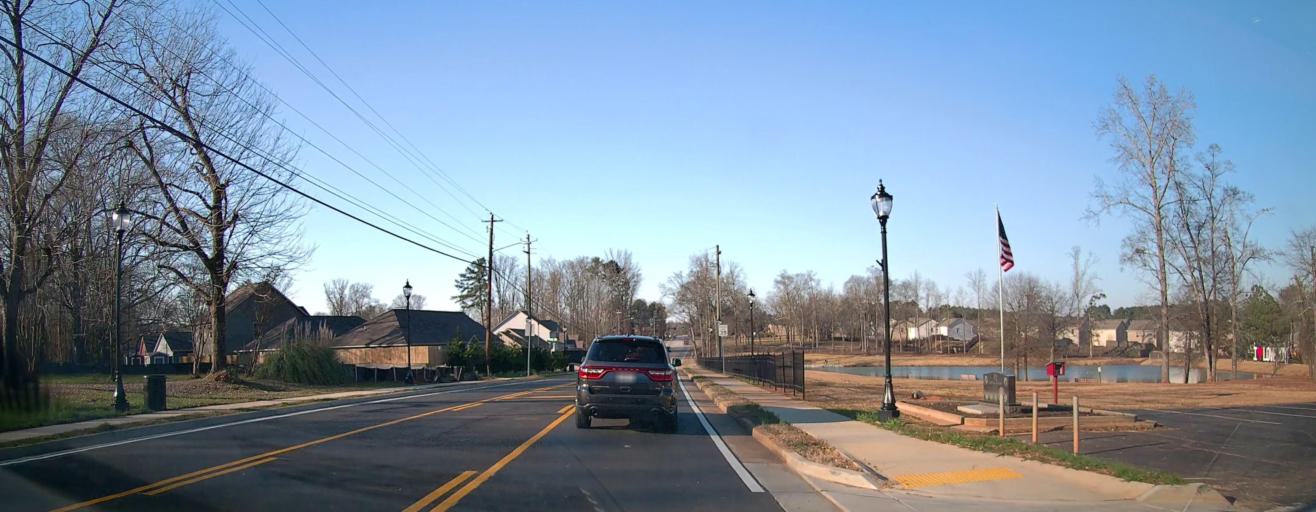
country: US
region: Georgia
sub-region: Clayton County
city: Lovejoy
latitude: 33.4384
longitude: -84.3149
